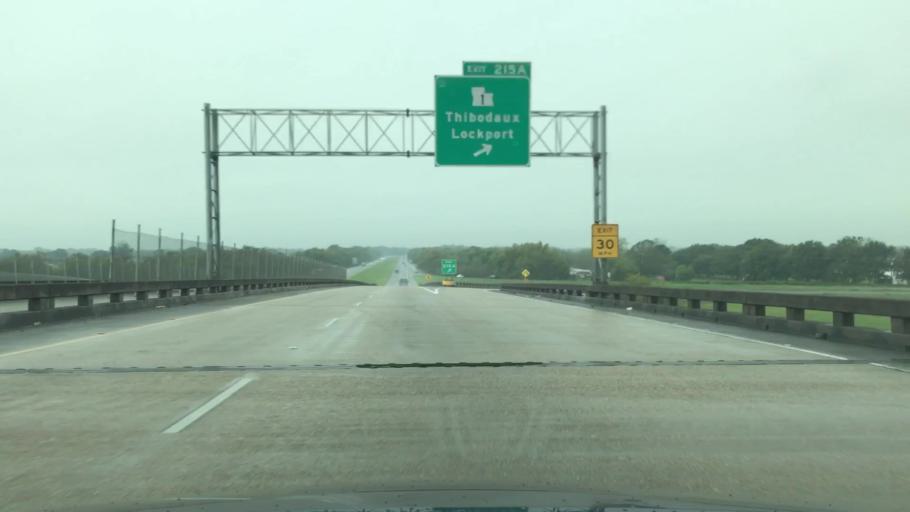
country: US
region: Louisiana
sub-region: Lafourche Parish
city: Raceland
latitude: 29.7073
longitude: -90.5727
